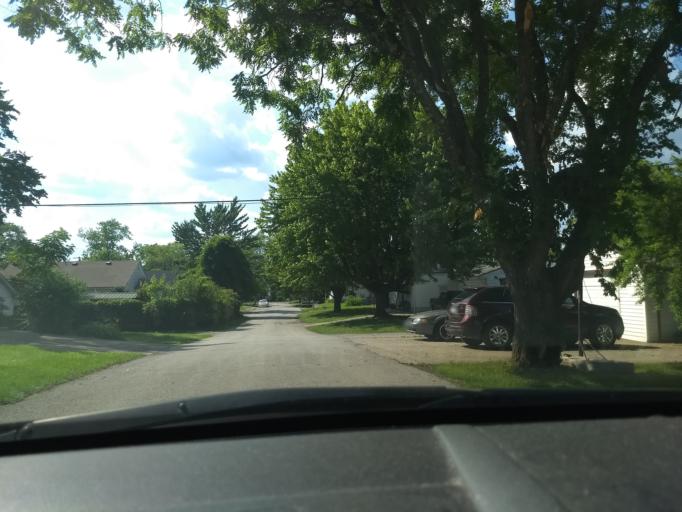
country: US
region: Indiana
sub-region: Floyd County
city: New Albany
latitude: 38.2971
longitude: -85.8301
